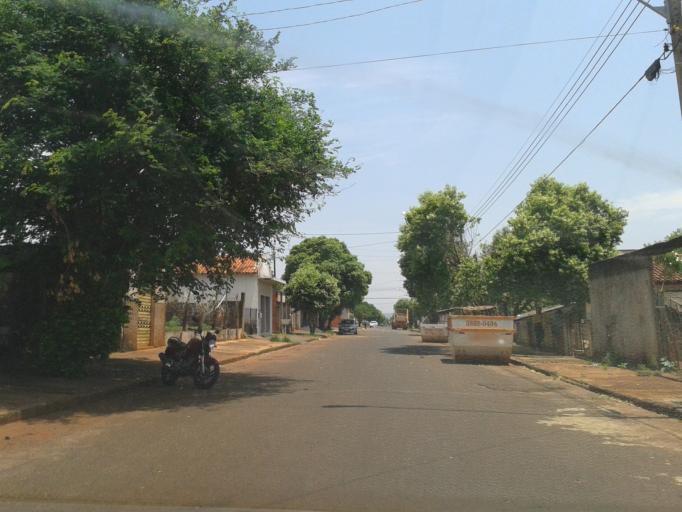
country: BR
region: Minas Gerais
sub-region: Ituiutaba
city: Ituiutaba
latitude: -18.9882
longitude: -49.4455
